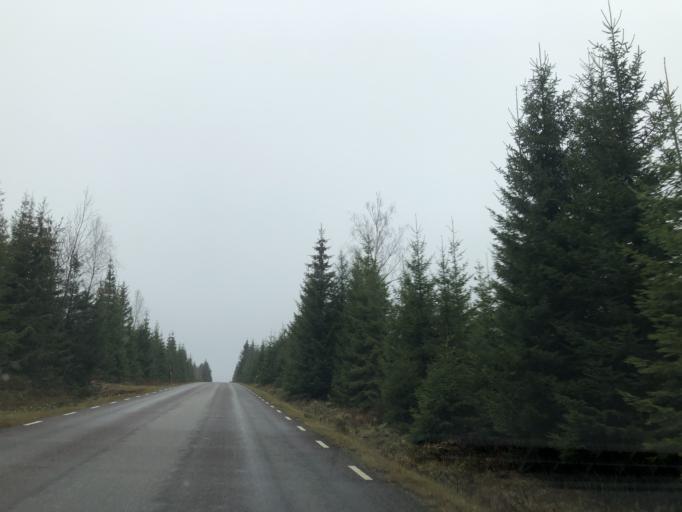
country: SE
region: Vaestra Goetaland
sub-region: Ulricehamns Kommun
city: Ulricehamn
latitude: 57.7348
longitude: 13.5427
